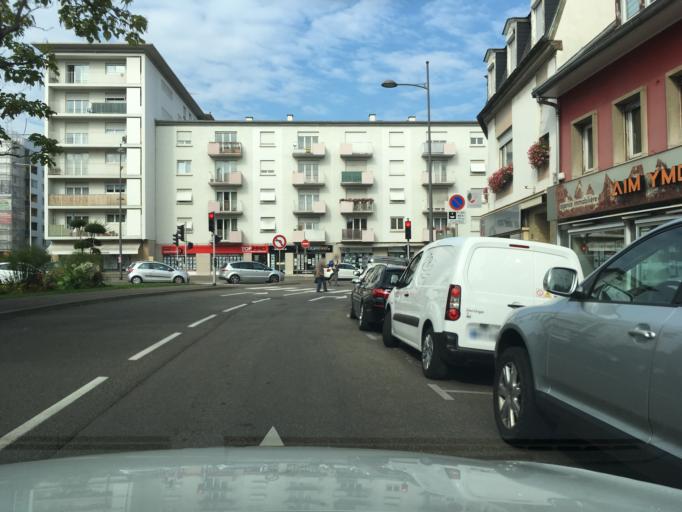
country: FR
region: Alsace
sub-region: Departement du Haut-Rhin
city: Colmar
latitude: 48.0787
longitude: 7.3525
